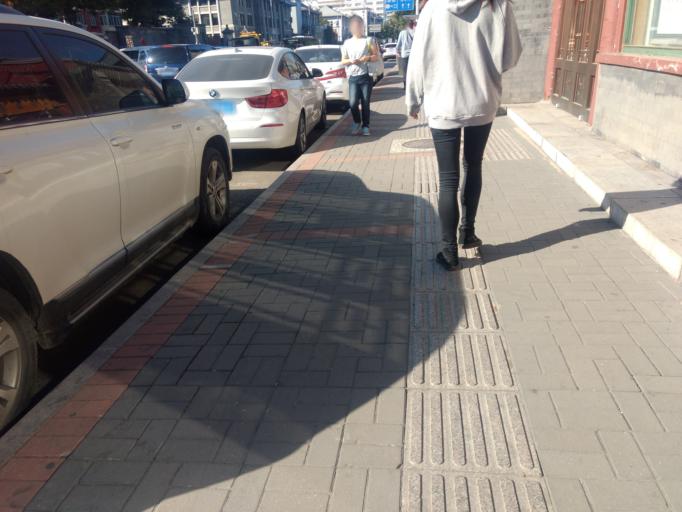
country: CN
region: Beijing
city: Beijing
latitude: 39.8944
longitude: 116.3783
